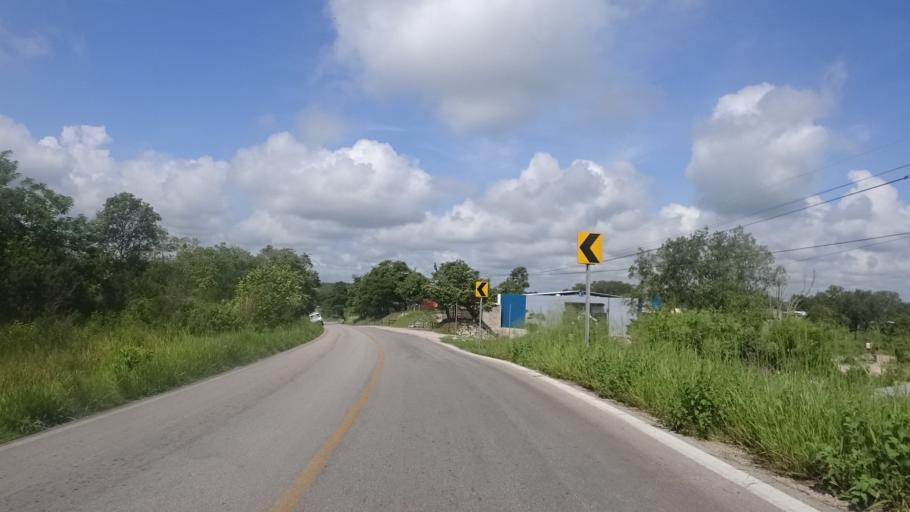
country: MX
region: Chiapas
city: Palenque
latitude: 17.5533
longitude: -91.9902
